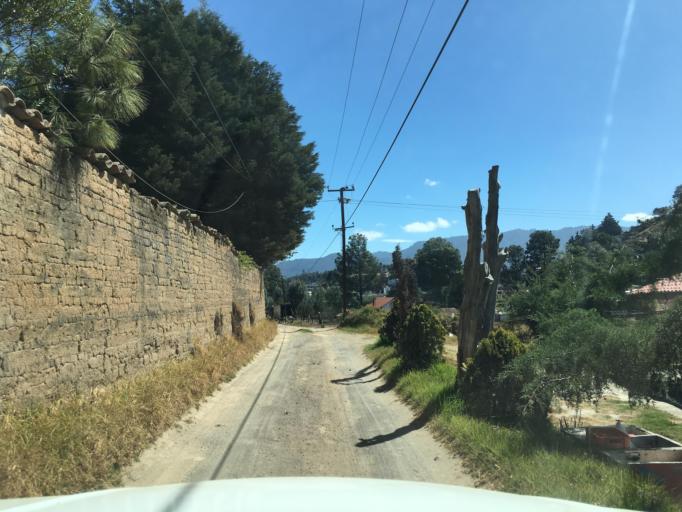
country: GT
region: Quetzaltenango
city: Quetzaltenango
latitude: 14.8446
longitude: -91.4927
